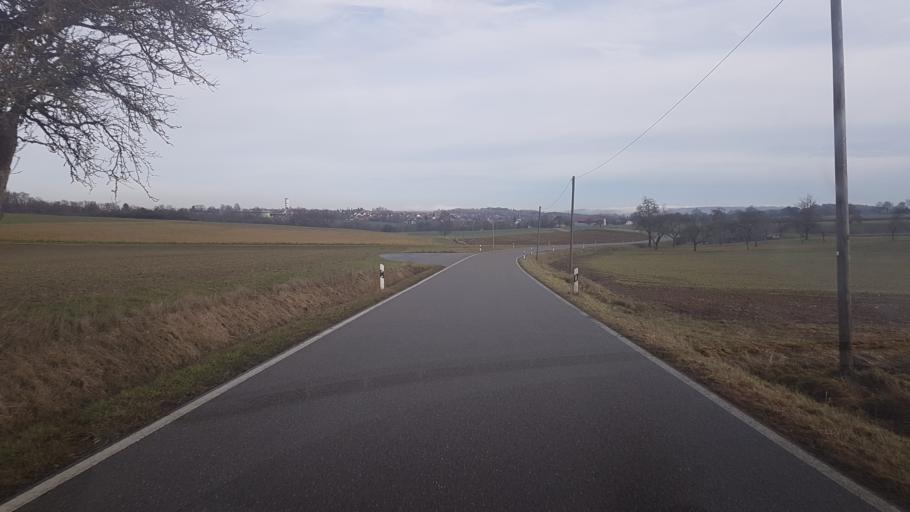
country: DE
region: Baden-Wuerttemberg
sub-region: Regierungsbezirk Stuttgart
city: Wallhausen
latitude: 49.2089
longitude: 10.0464
